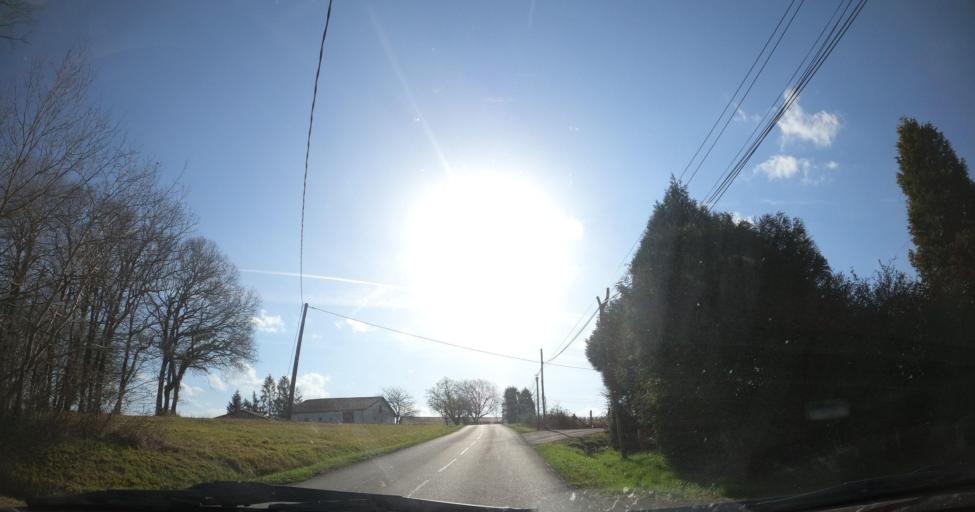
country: FR
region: Aquitaine
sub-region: Departement des Pyrenees-Atlantiques
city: Briscous
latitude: 43.4509
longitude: -1.3703
